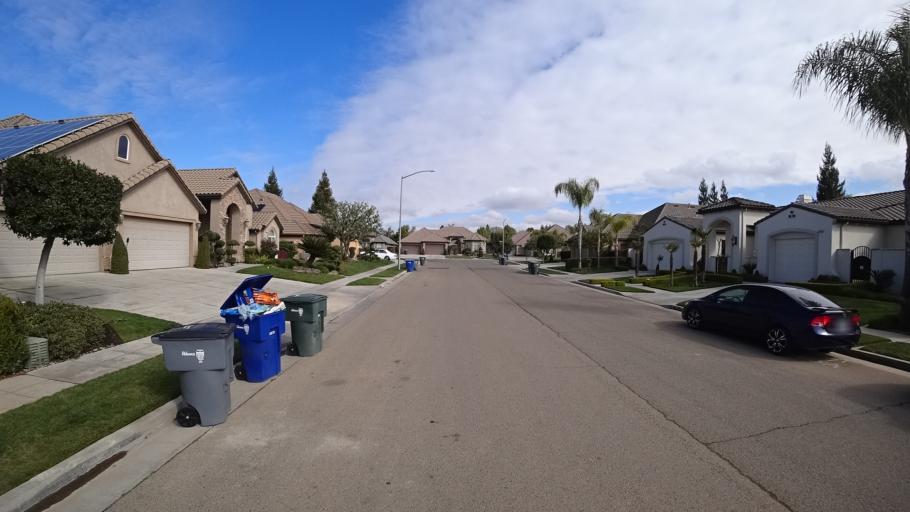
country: US
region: California
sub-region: Fresno County
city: West Park
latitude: 36.8278
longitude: -119.8666
